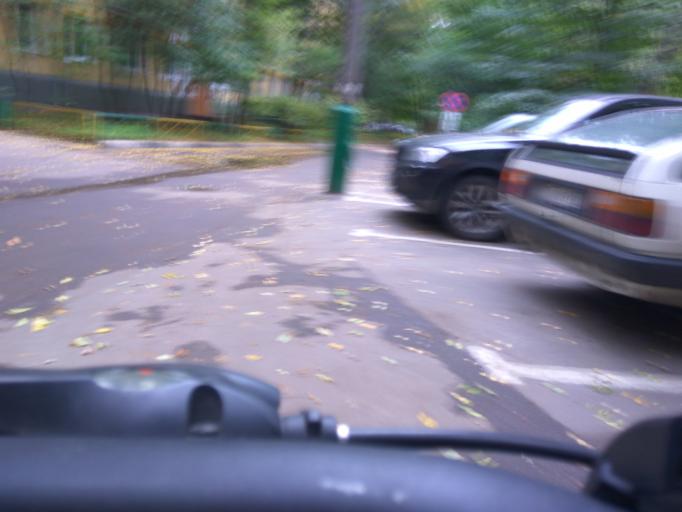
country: RU
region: Moscow
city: Leonovo
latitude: 55.8509
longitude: 37.6427
